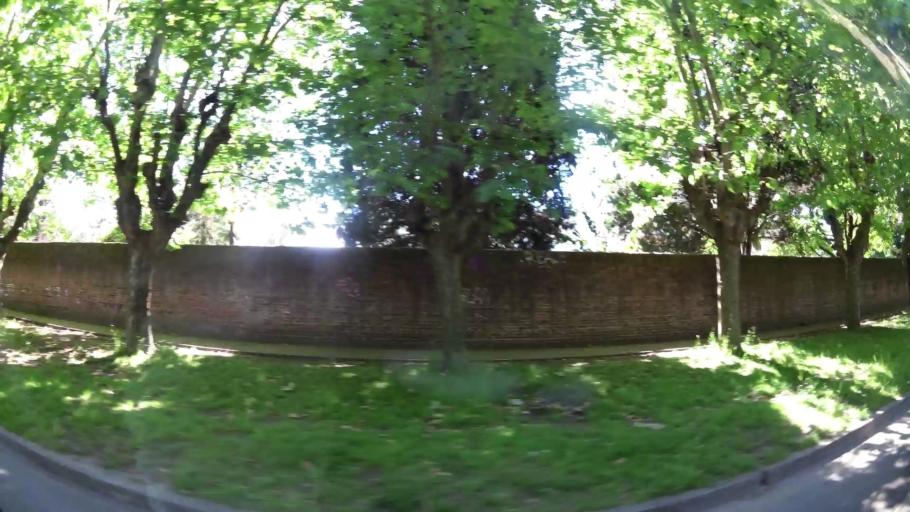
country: AR
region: Buenos Aires
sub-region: Partido de Almirante Brown
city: Adrogue
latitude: -34.7924
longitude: -58.3632
